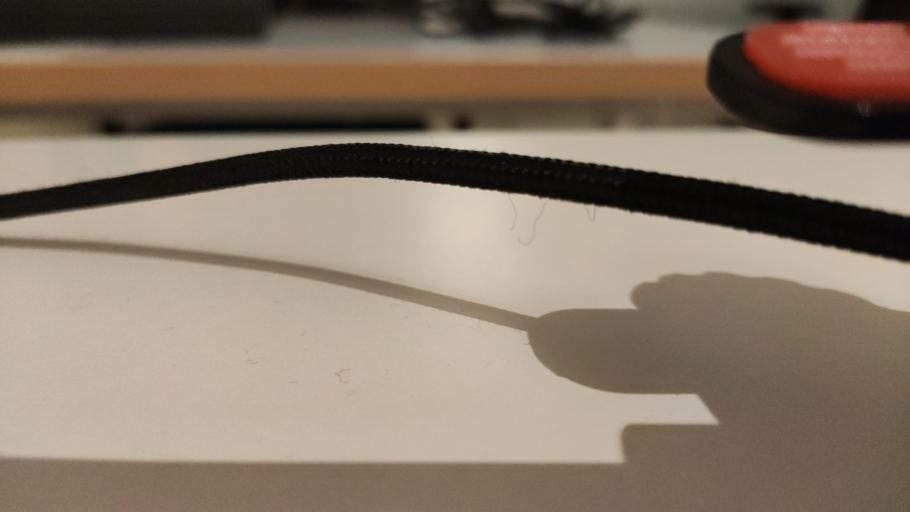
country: RU
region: Moskovskaya
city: Semkhoz
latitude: 56.3886
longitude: 38.0515
